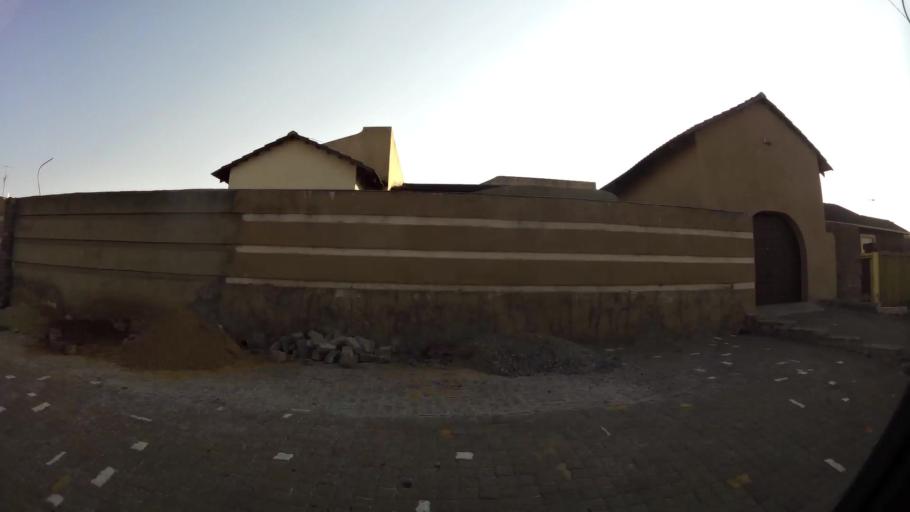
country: ZA
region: Gauteng
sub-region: City of Johannesburg Metropolitan Municipality
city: Soweto
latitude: -26.2566
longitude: 27.9573
